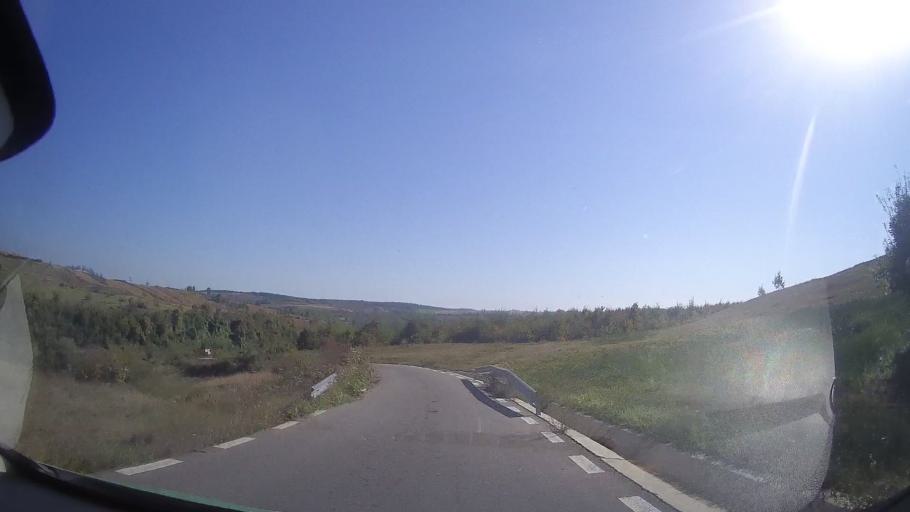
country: RO
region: Timis
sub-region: Comuna Ohaba Lunga
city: Ohaba Lunga
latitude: 45.9085
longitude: 21.9728
